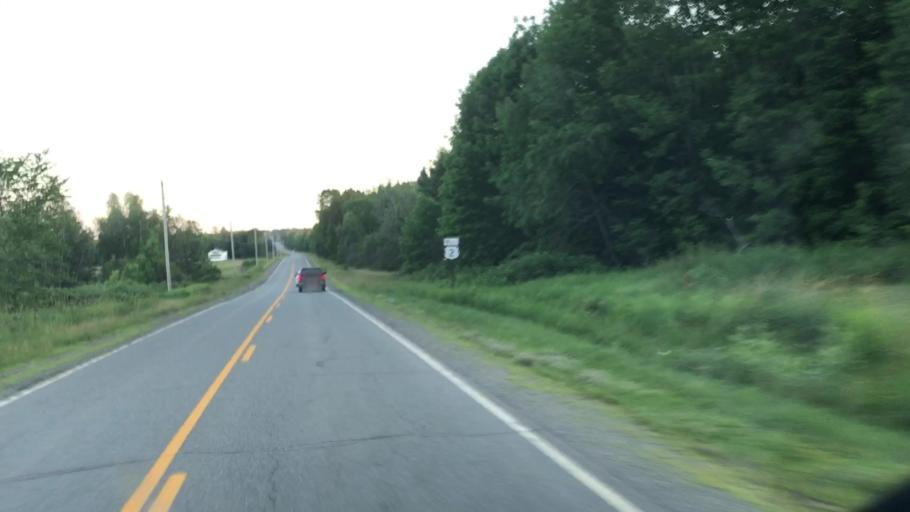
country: US
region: Maine
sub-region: Penobscot County
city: Medway
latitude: 45.6148
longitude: -68.3037
